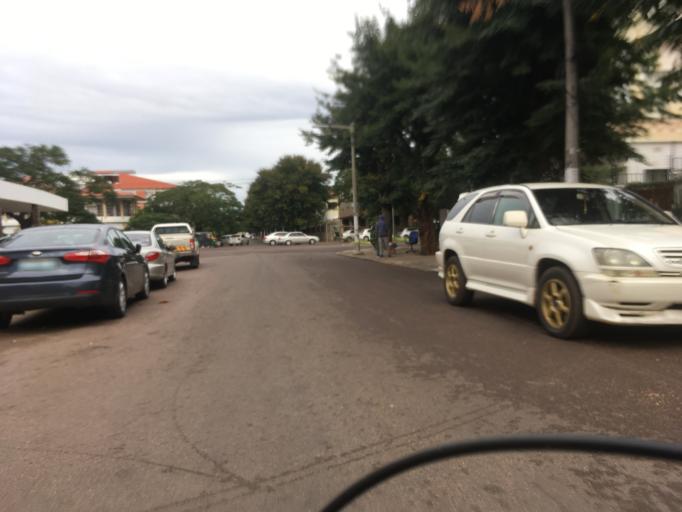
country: MZ
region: Maputo City
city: Maputo
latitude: -25.9638
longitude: 32.5911
